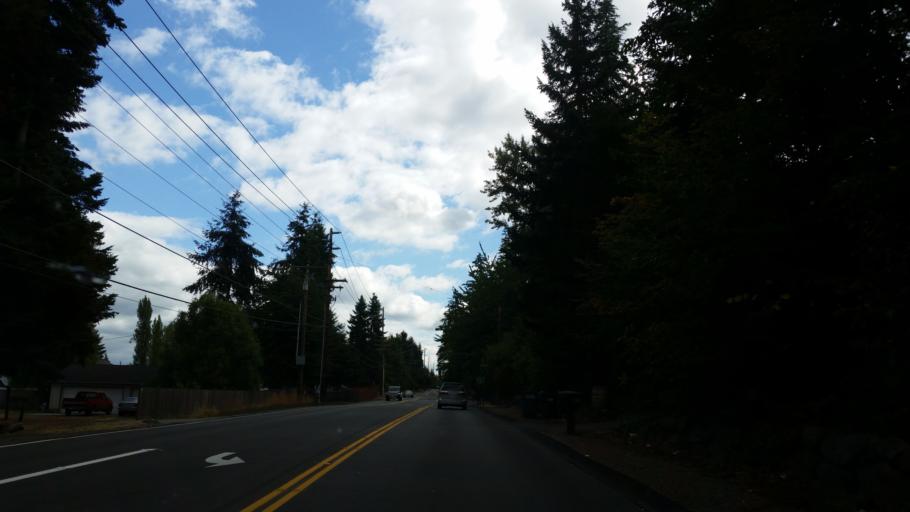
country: US
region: Washington
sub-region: Pierce County
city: Bonney Lake
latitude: 47.2280
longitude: -122.1443
